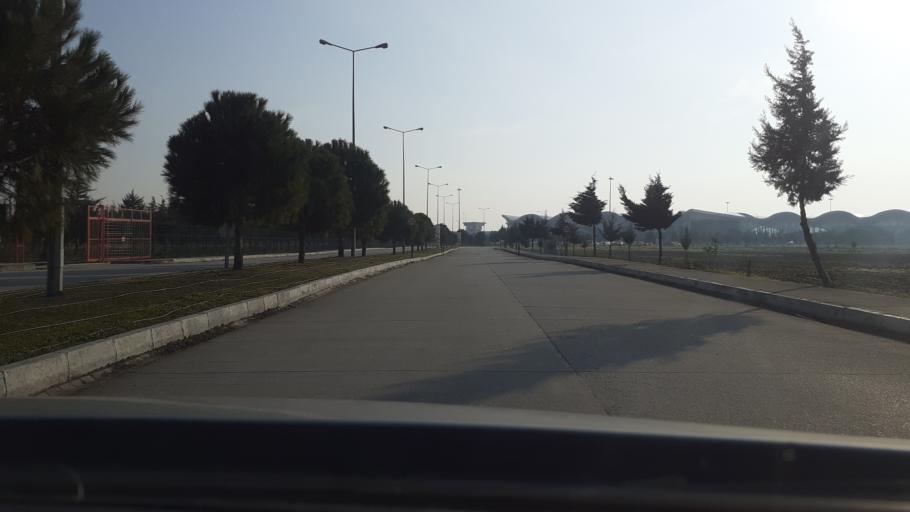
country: TR
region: Hatay
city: Serinyol
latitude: 36.3644
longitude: 36.2771
